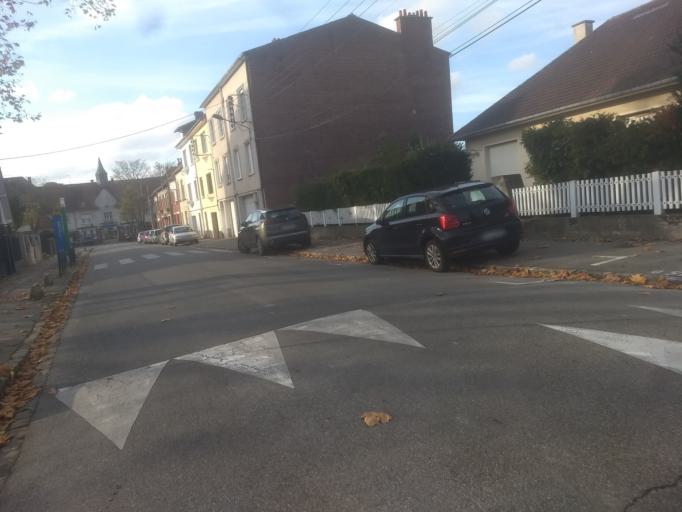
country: FR
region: Nord-Pas-de-Calais
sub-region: Departement du Pas-de-Calais
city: Arras
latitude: 50.2795
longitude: 2.7806
